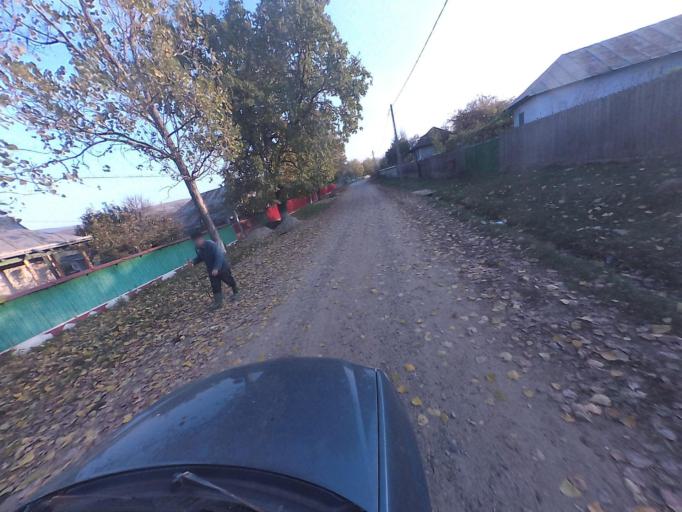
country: RO
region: Vaslui
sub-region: Comuna Bacesti
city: Bacesti
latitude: 46.8042
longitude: 27.2246
